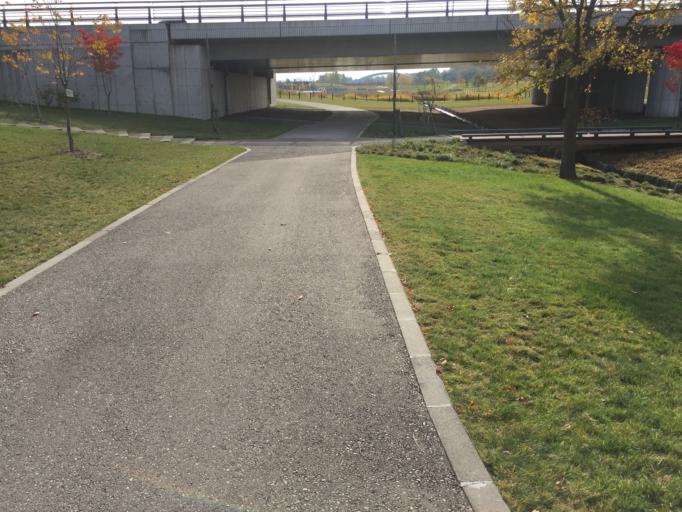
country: JP
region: Hokkaido
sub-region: Asahikawa-shi
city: Asahikawa
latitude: 43.7617
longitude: 142.3595
